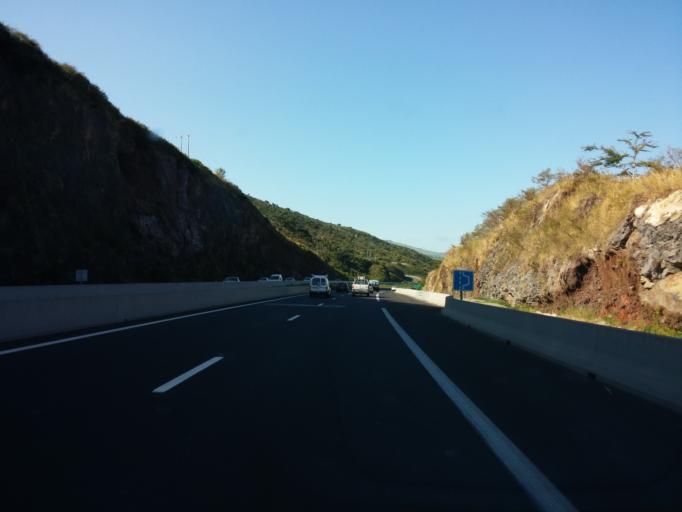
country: RE
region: Reunion
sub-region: Reunion
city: Trois-Bassins
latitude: -21.1073
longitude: 55.2732
